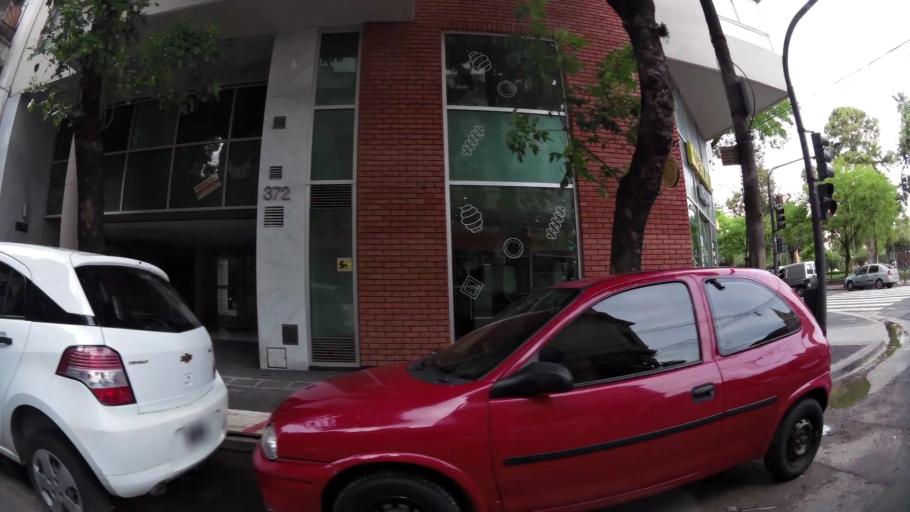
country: AR
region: Buenos Aires F.D.
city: Villa Santa Rita
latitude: -34.6321
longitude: -58.4566
